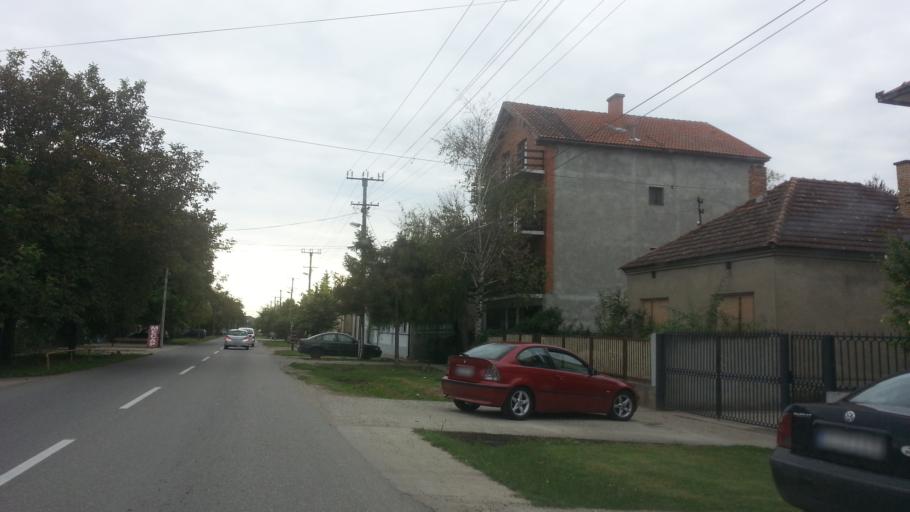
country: RS
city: Stari Banovci
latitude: 44.9906
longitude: 20.2887
